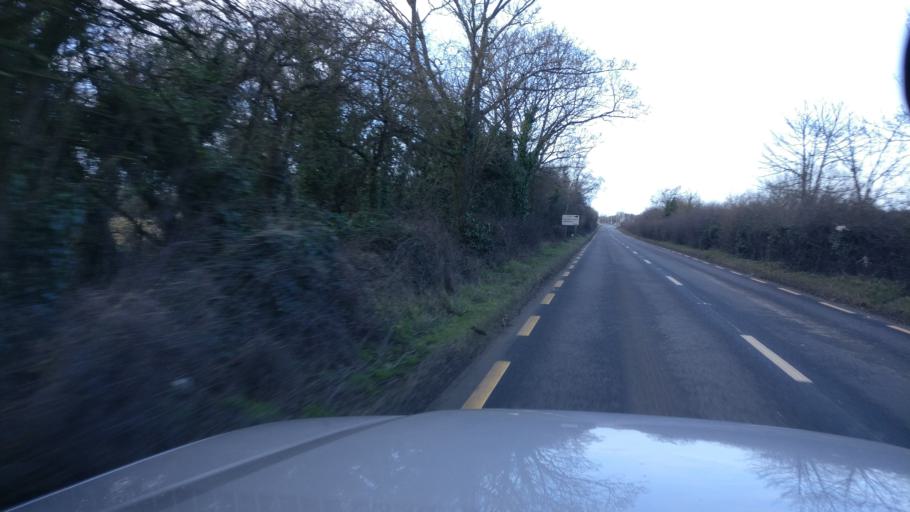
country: IE
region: Leinster
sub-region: Laois
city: Portlaoise
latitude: 53.0618
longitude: -7.3250
